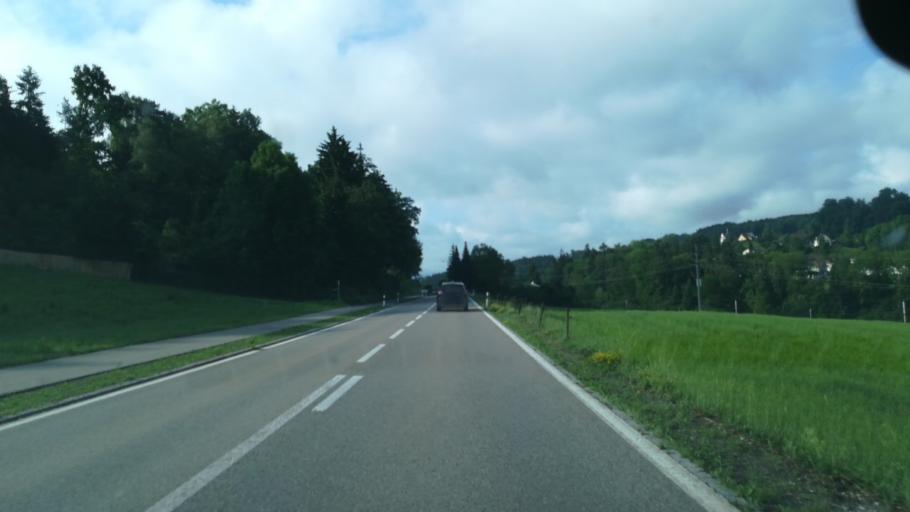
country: CH
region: Thurgau
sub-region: Weinfelden District
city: Sulgen
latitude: 47.5097
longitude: 9.2105
